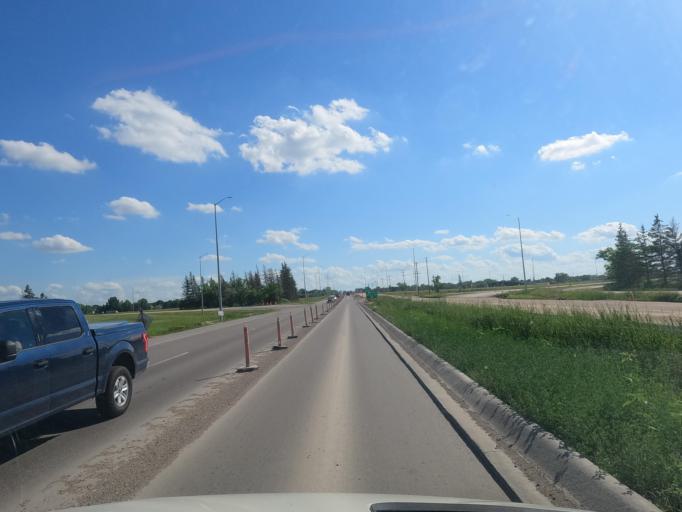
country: CA
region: Manitoba
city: Winnipeg
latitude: 49.9752
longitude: -97.0712
